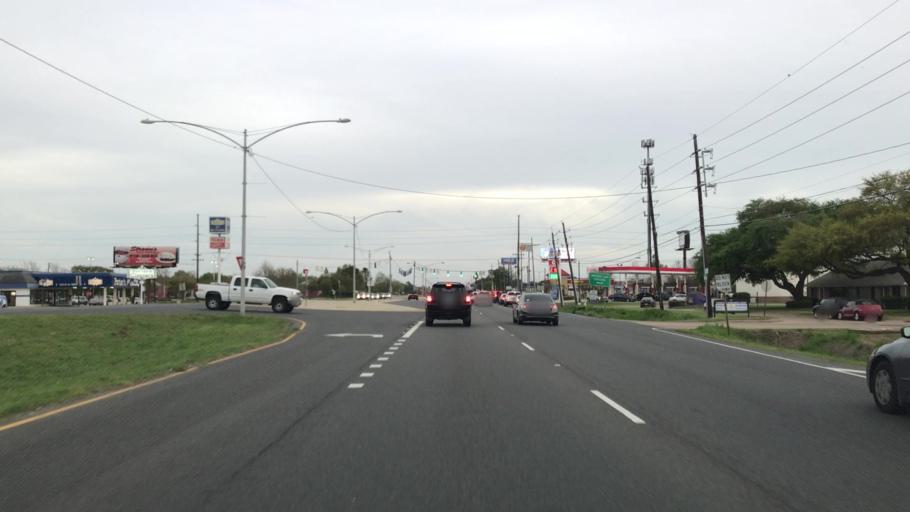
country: US
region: Louisiana
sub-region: Bossier Parish
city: Bossier City
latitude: 32.4334
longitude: -93.7129
